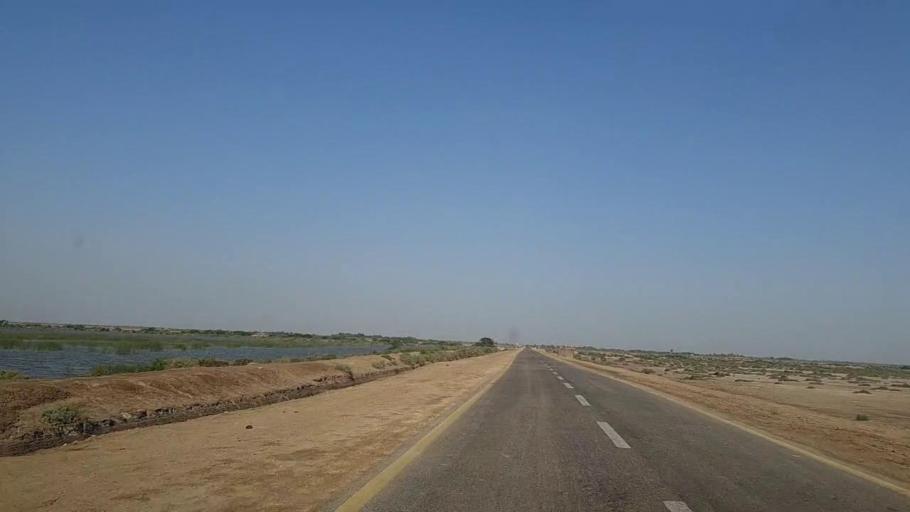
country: PK
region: Sindh
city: Jati
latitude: 24.4415
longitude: 68.3209
